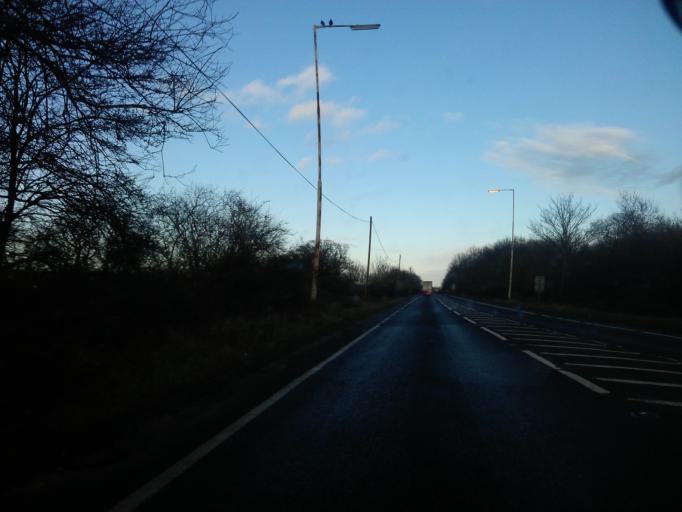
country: GB
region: England
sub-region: Suffolk
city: Shotley Gate
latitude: 51.9293
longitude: 1.2207
